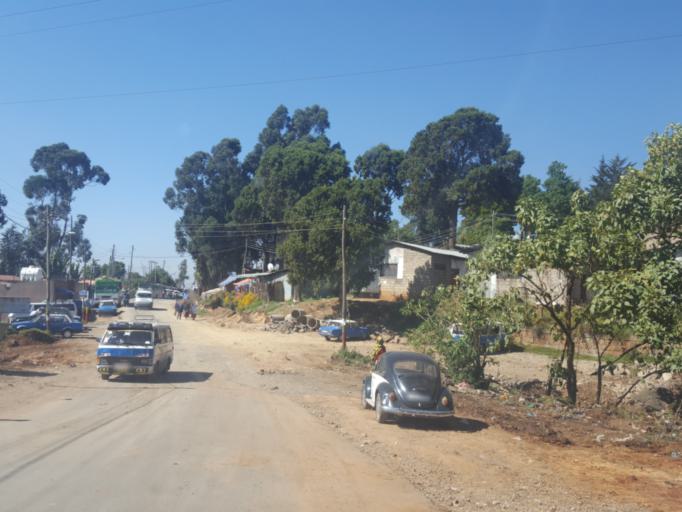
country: ET
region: Adis Abeba
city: Addis Ababa
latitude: 9.0645
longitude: 38.7454
